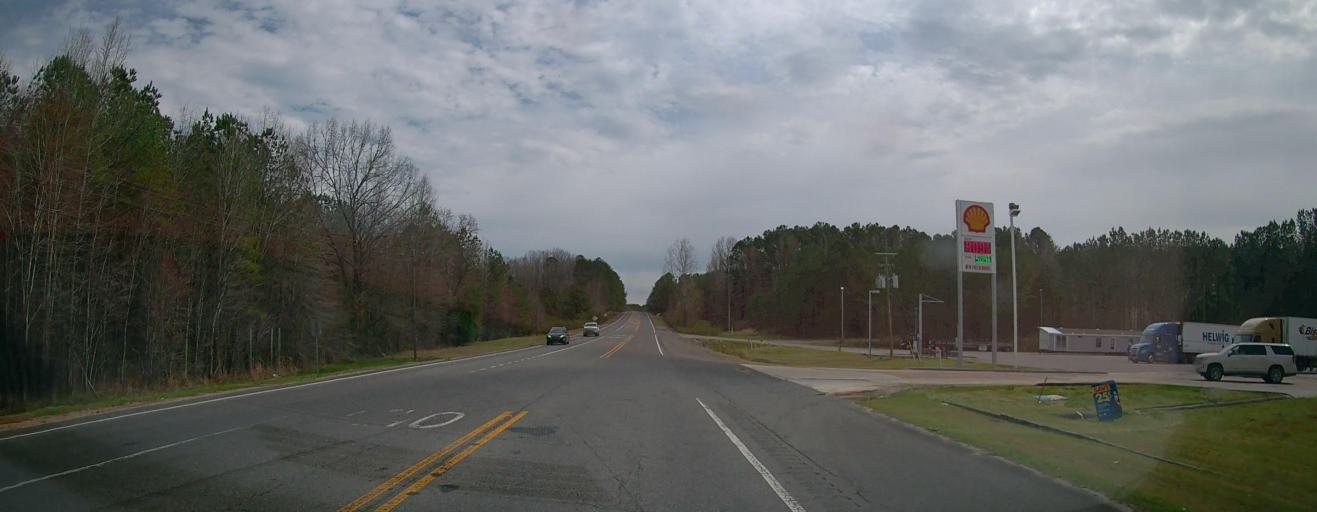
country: US
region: Alabama
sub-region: Marion County
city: Hamilton
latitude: 34.0681
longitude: -87.9732
